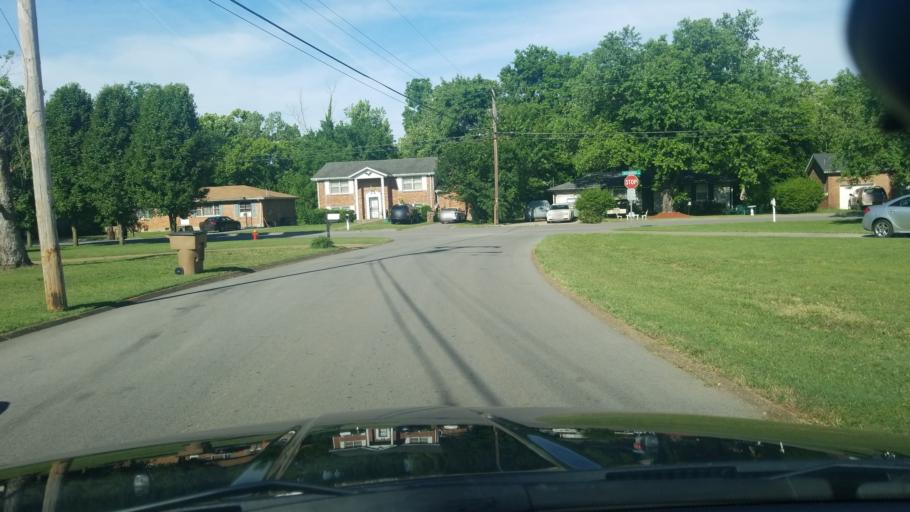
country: US
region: Tennessee
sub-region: Davidson County
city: Nashville
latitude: 36.2329
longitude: -86.7762
